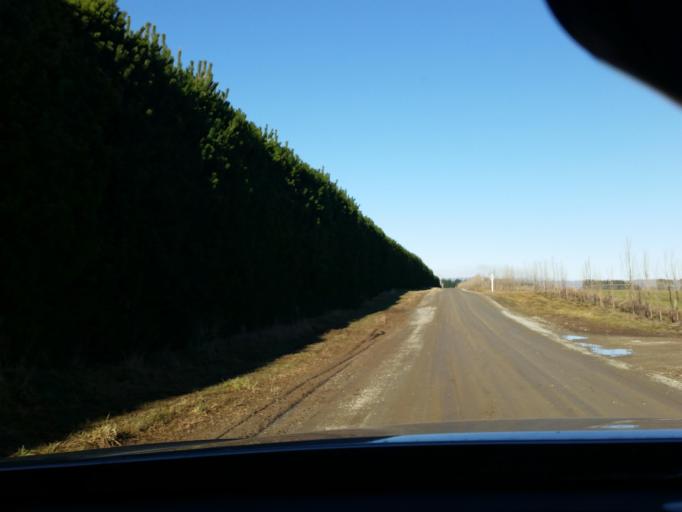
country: NZ
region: Southland
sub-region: Gore District
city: Gore
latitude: -45.7920
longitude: 168.7213
